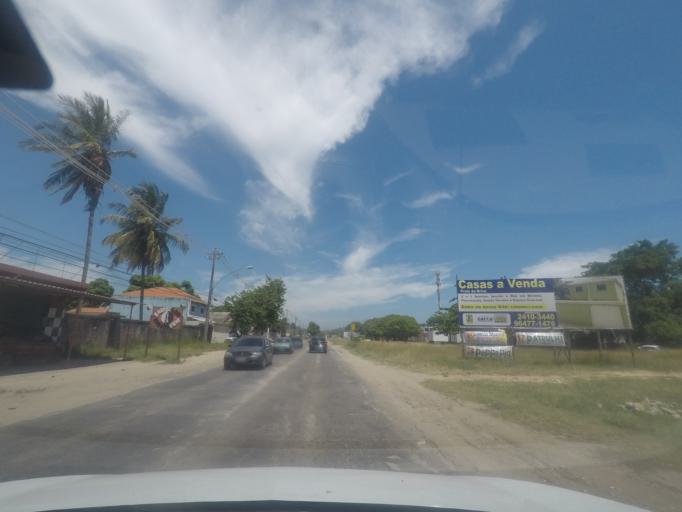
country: BR
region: Rio de Janeiro
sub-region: Itaguai
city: Itaguai
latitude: -22.9812
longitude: -43.6652
